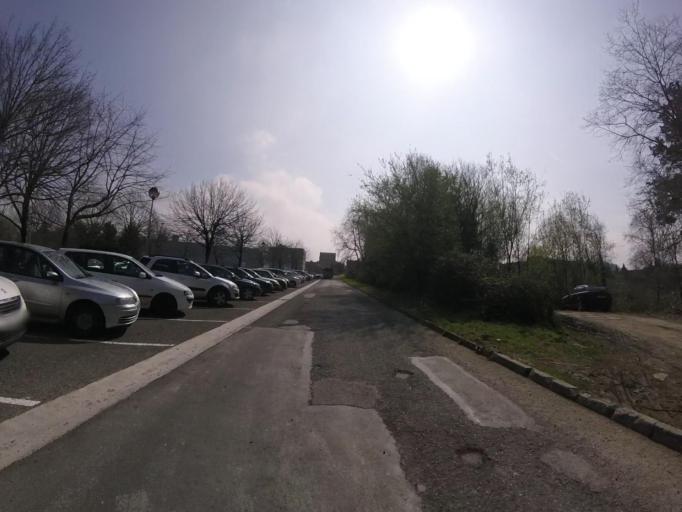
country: ES
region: Basque Country
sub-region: Provincia de Guipuzcoa
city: Hernani
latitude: 43.2895
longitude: -1.9832
